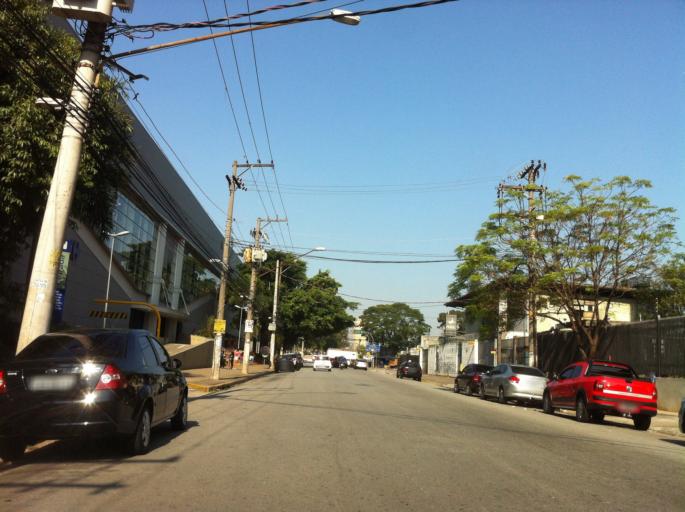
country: BR
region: Sao Paulo
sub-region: Osasco
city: Osasco
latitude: -23.5411
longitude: -46.7318
